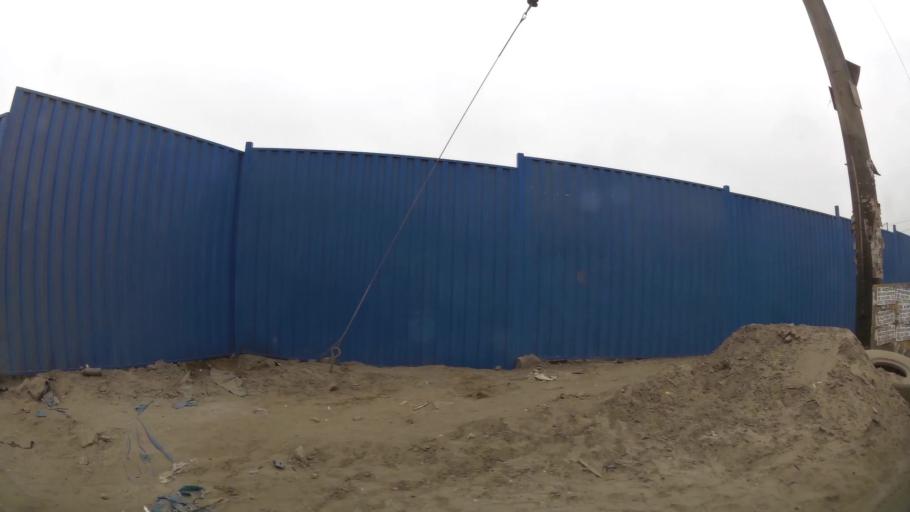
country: PE
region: Lima
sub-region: Lima
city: Surco
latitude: -12.1984
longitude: -76.9638
